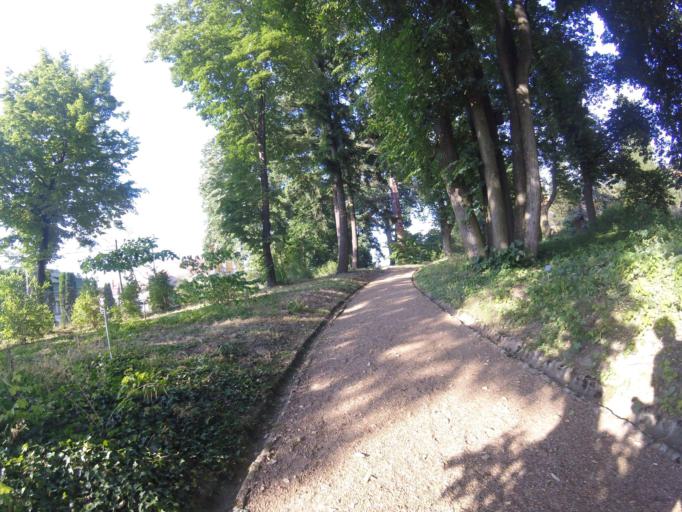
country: HU
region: Baranya
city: Sellye
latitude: 45.8707
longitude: 17.8453
